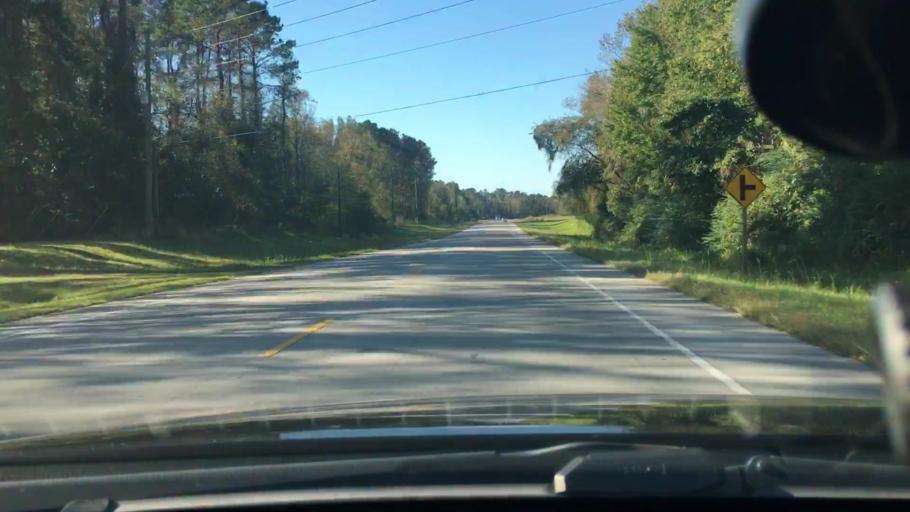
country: US
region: North Carolina
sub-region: Craven County
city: Trent Woods
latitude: 35.1694
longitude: -77.1256
